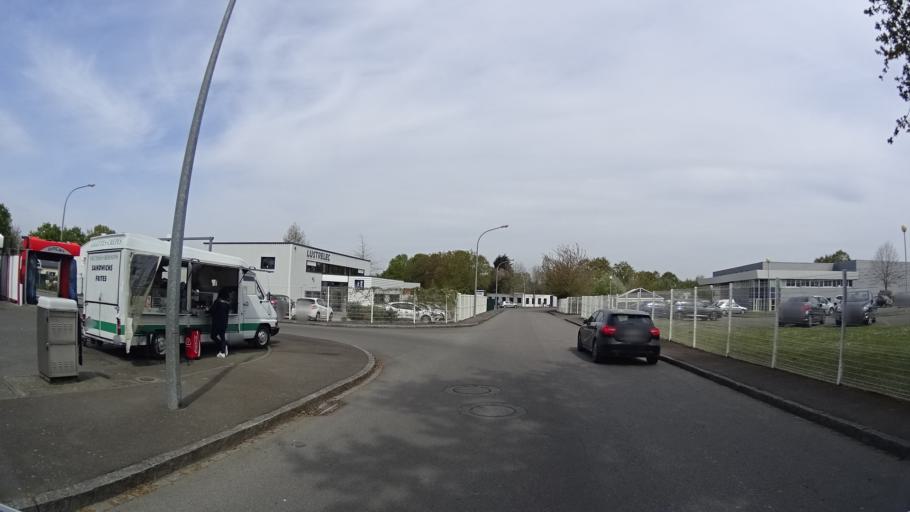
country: FR
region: Brittany
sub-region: Departement d'Ille-et-Vilaine
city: Bruz
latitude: 48.0343
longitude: -1.7283
